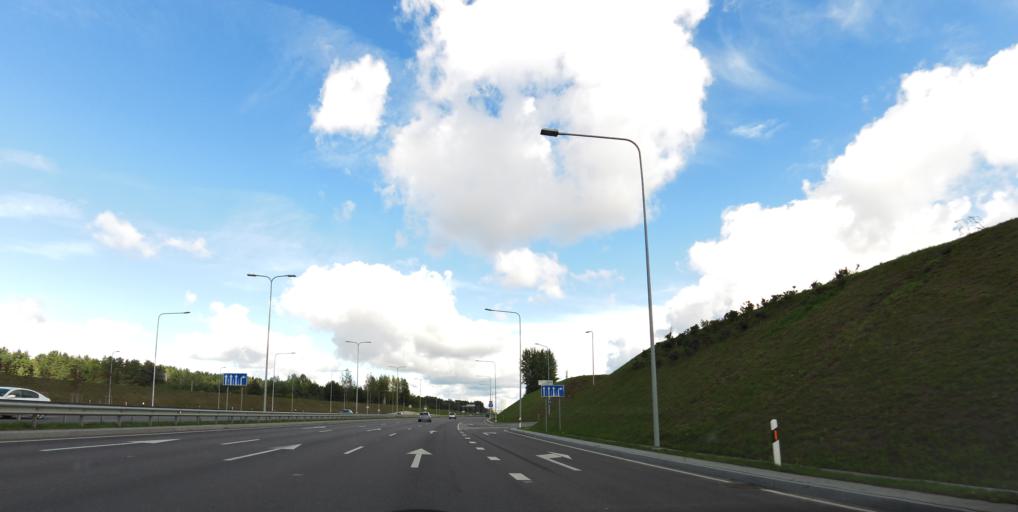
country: LT
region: Vilnius County
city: Pilaite
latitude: 54.6840
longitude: 25.1950
